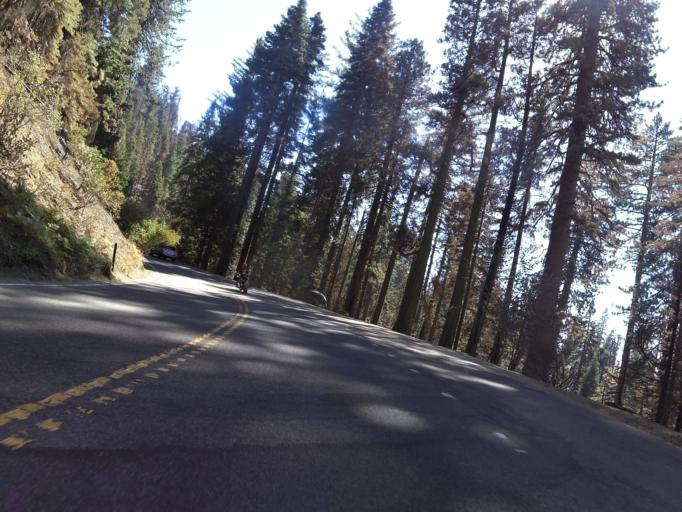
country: US
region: California
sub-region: Mariposa County
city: Yosemite Valley
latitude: 37.6694
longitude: -119.7107
